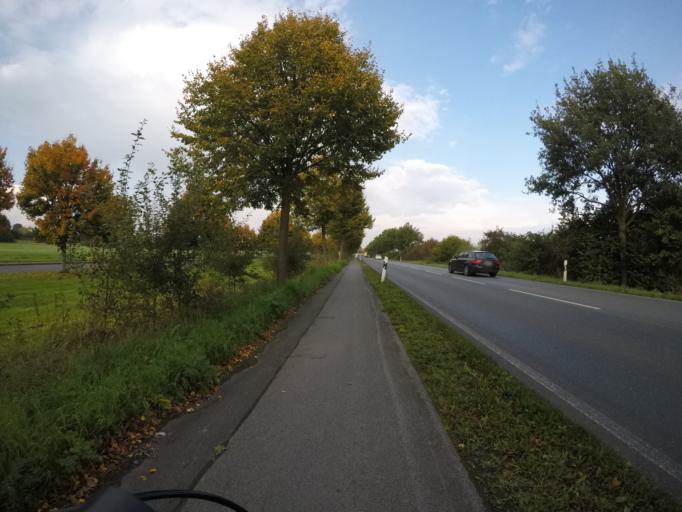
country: DE
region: North Rhine-Westphalia
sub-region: Regierungsbezirk Detmold
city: Herford
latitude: 52.1006
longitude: 8.6402
